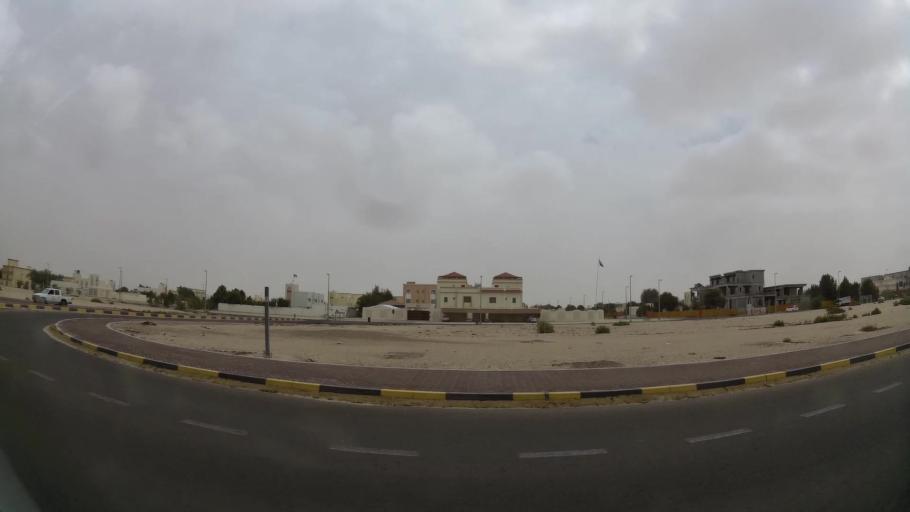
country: AE
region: Abu Dhabi
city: Abu Dhabi
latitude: 24.3956
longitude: 54.7178
